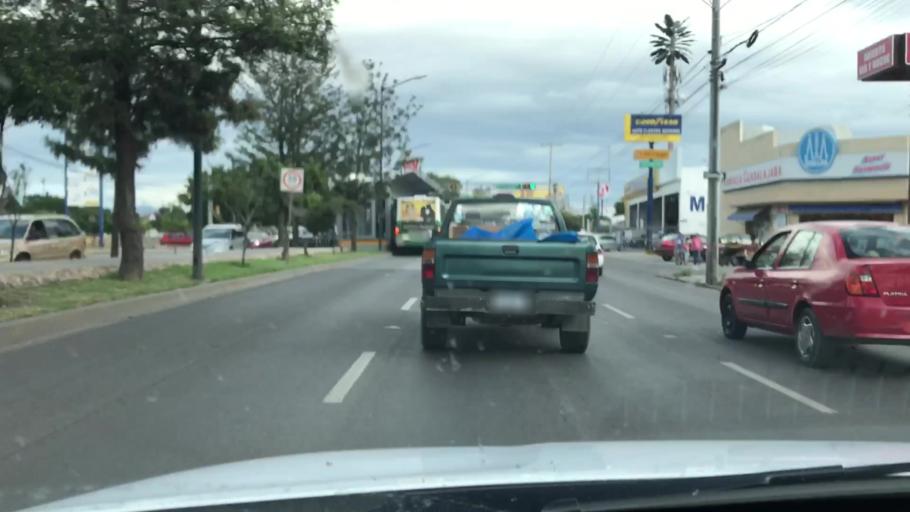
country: MX
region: Guanajuato
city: Leon
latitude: 21.1005
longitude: -101.6729
